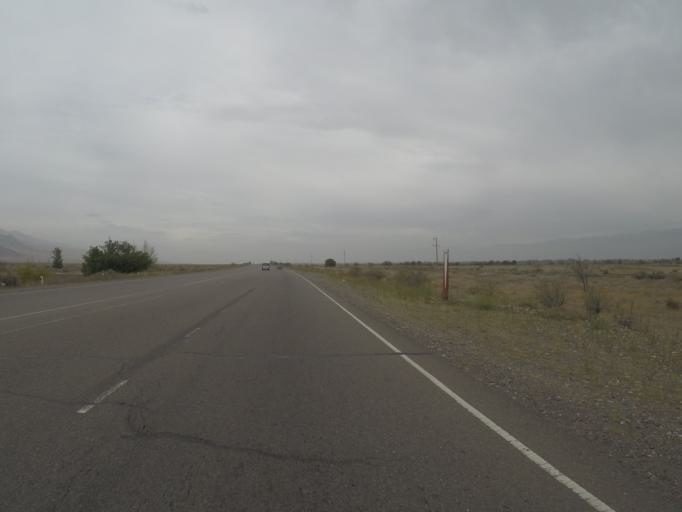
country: KG
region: Chuy
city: Tokmok
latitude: 42.8303
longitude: 75.4620
